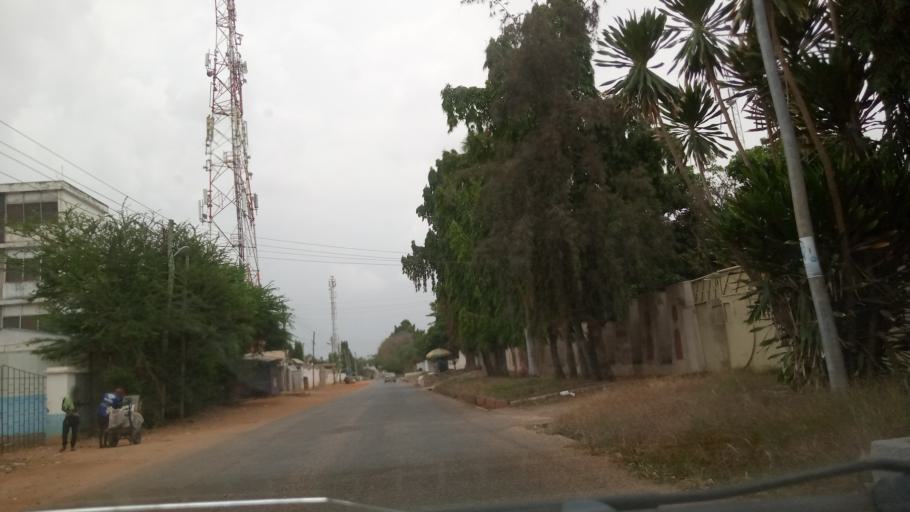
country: GH
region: Greater Accra
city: Accra
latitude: 5.6081
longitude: -0.1862
